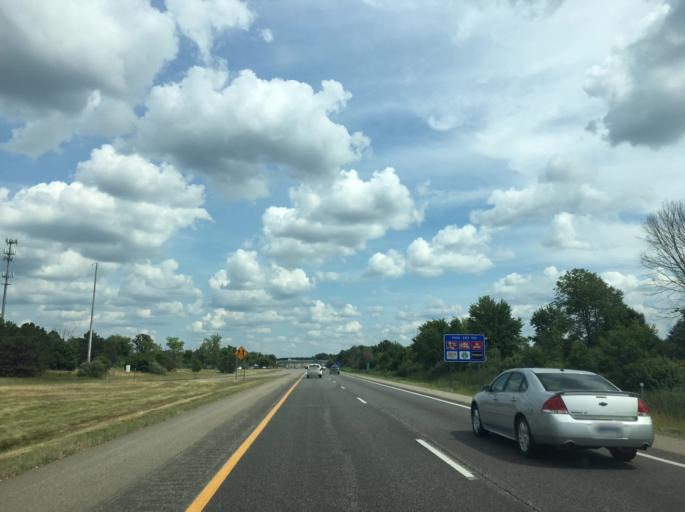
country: US
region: Michigan
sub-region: Genesee County
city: Grand Blanc
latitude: 42.9192
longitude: -83.6800
